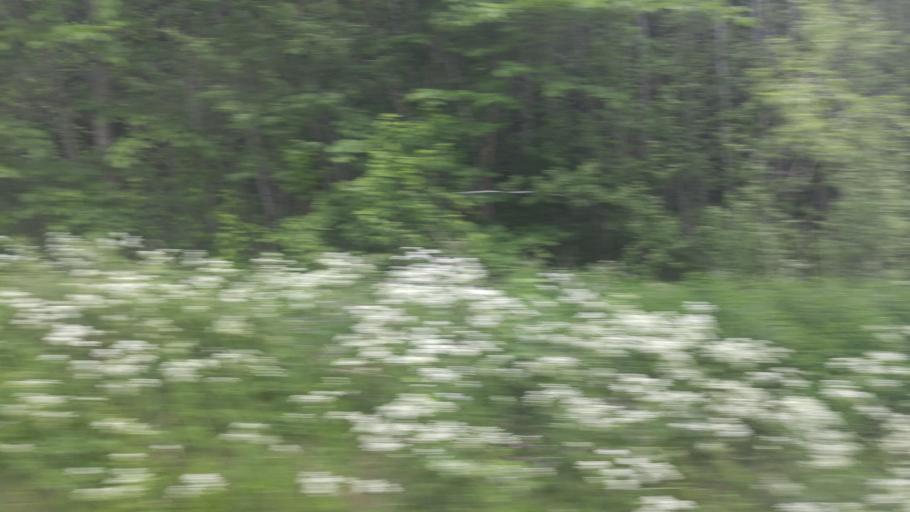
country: NO
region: Sor-Trondelag
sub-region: Midtre Gauldal
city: Storen
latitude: 63.0164
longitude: 10.4466
